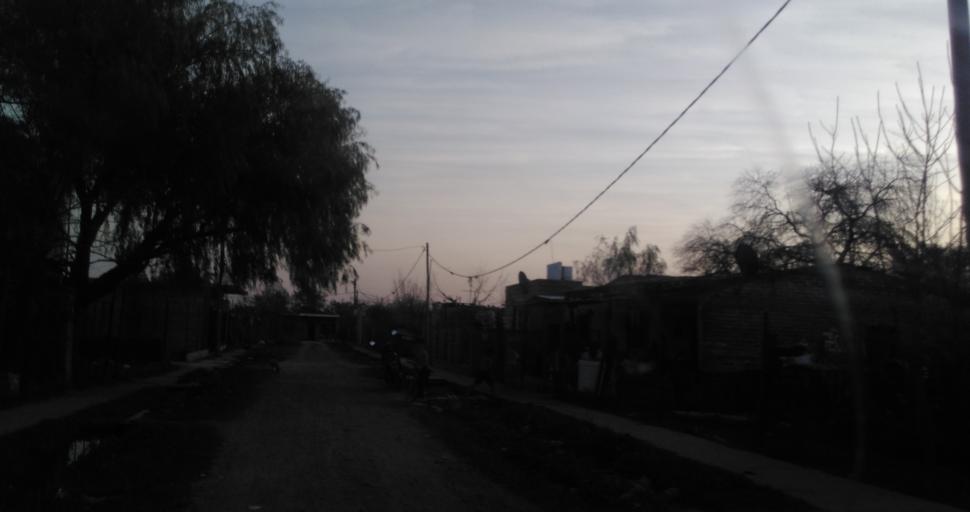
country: AR
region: Chaco
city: Resistencia
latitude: -27.4634
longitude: -59.0196
